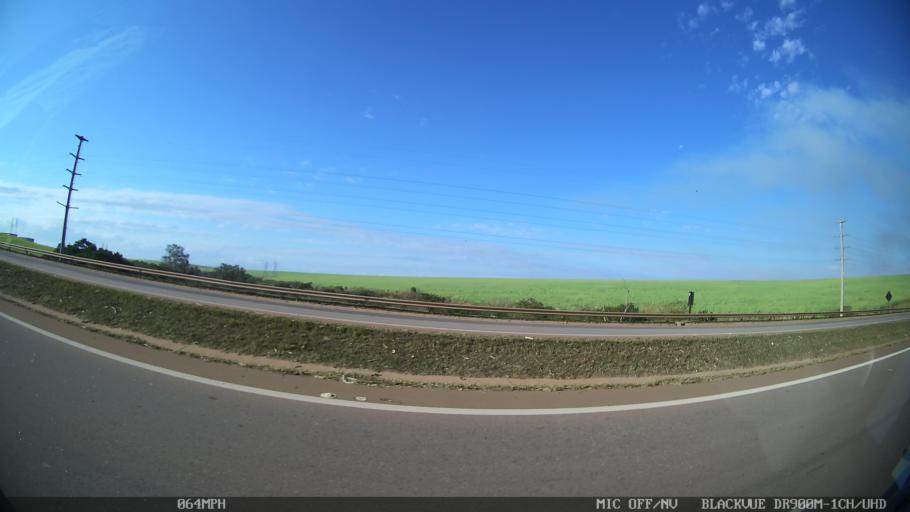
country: BR
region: Sao Paulo
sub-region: Piracicaba
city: Piracicaba
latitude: -22.6750
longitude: -47.5994
